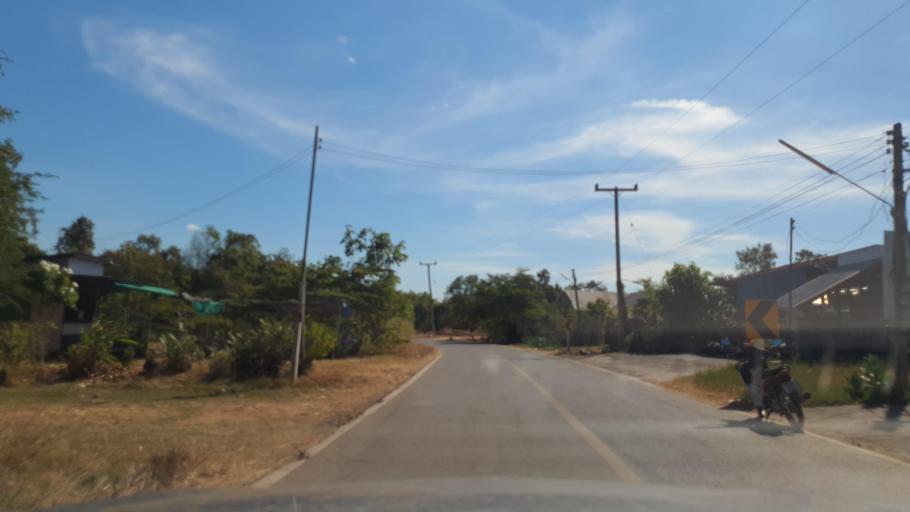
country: TH
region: Kalasin
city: Khao Wong
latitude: 16.6932
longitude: 104.1121
